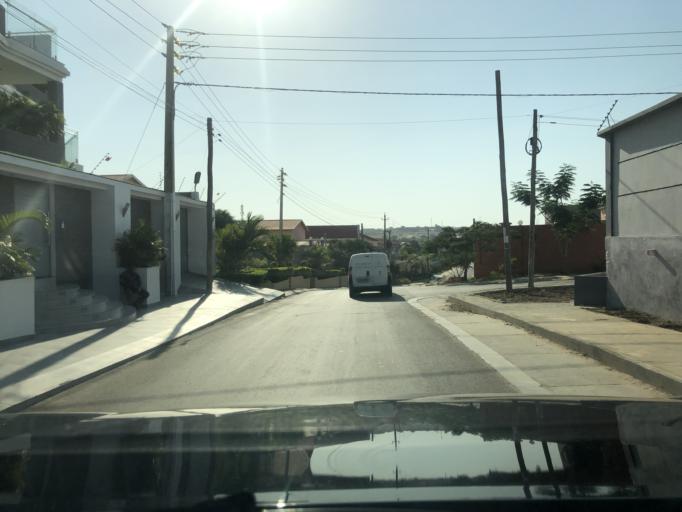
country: AO
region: Luanda
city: Luanda
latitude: -8.9068
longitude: 13.2225
